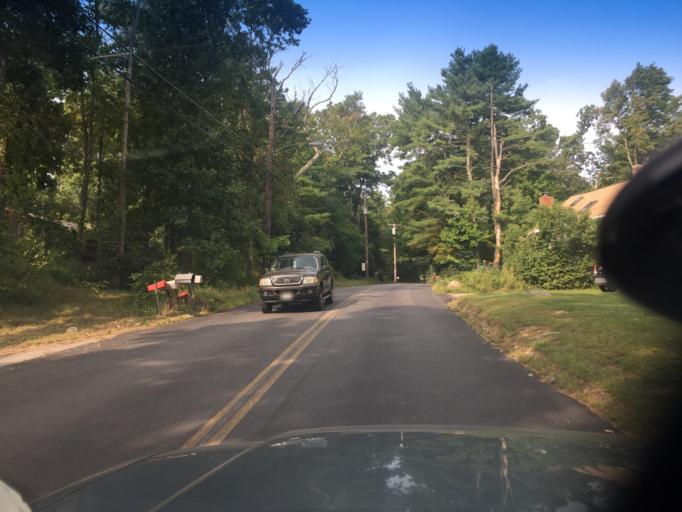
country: US
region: Massachusetts
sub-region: Norfolk County
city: Bellingham
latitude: 42.1309
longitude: -71.4523
